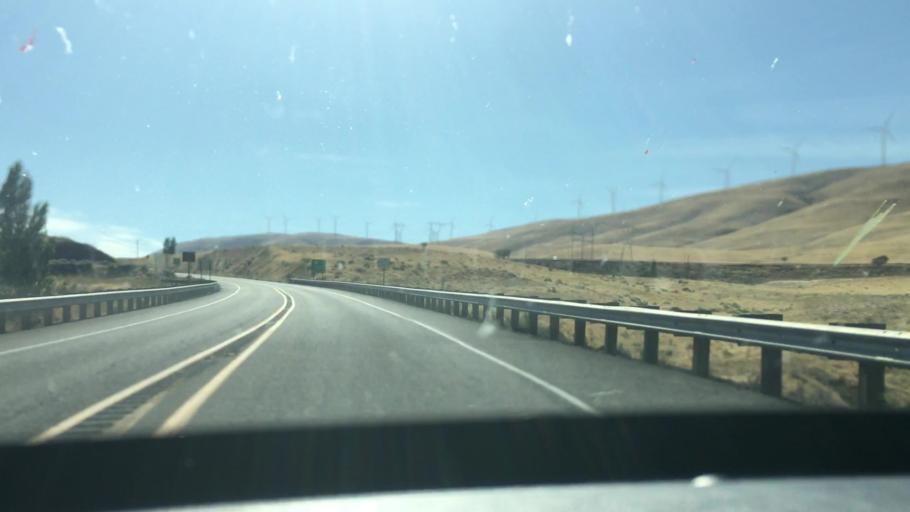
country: US
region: Washington
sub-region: Klickitat County
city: Goldendale
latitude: 45.6979
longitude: -120.8179
